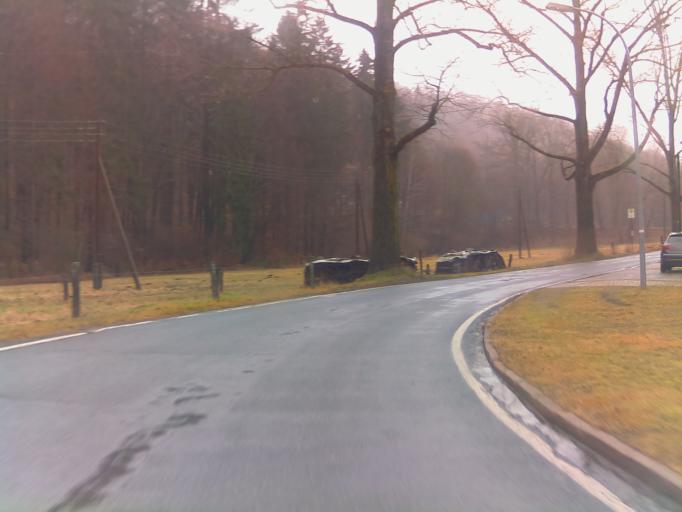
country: DE
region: Thuringia
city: Grafenroda
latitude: 50.7304
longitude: 10.7919
